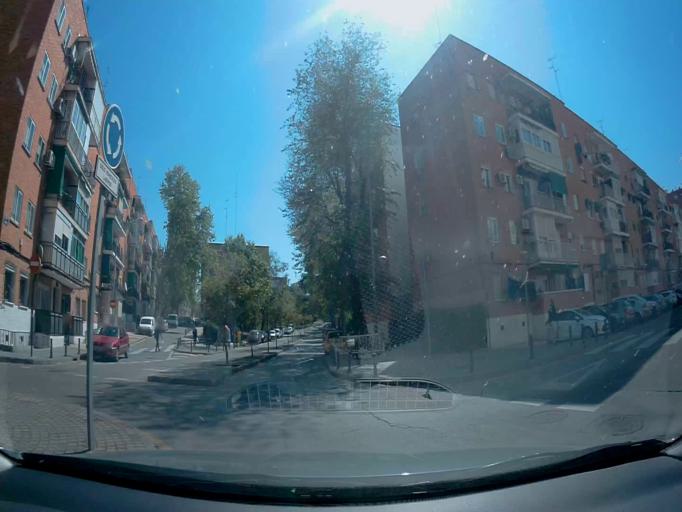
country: ES
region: Madrid
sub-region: Provincia de Madrid
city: Alcorcon
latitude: 40.3431
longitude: -3.8313
